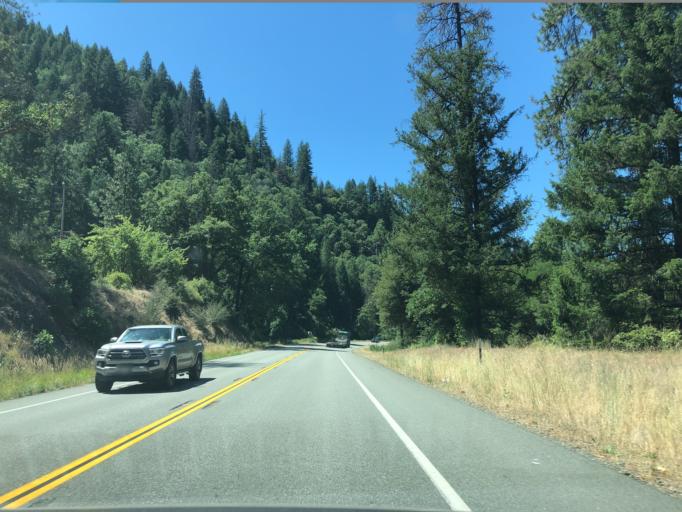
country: US
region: California
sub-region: Trinity County
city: Weaverville
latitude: 40.6845
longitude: -122.9346
